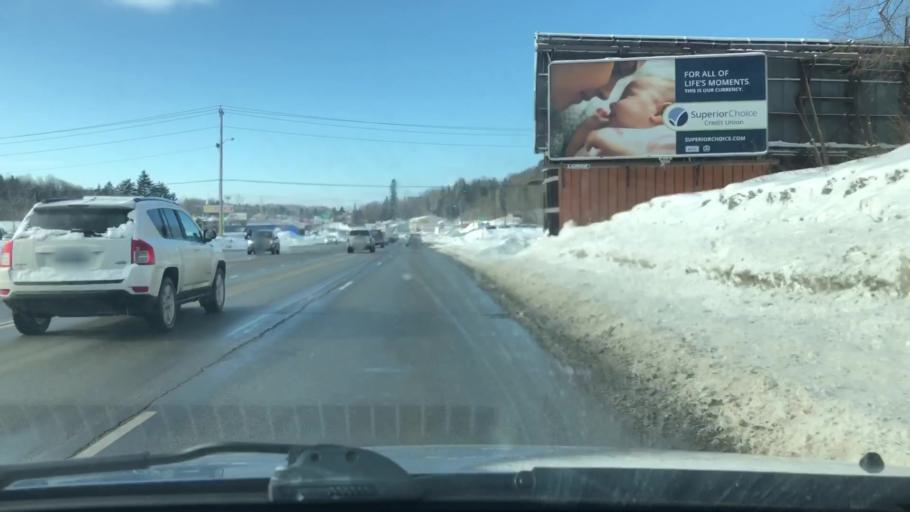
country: US
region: Minnesota
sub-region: Saint Louis County
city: Duluth
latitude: 46.8001
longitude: -92.1206
